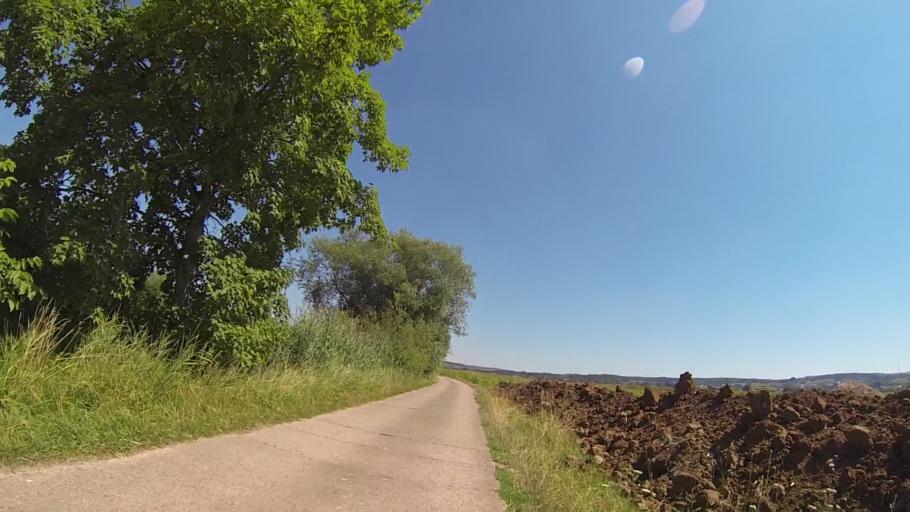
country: LU
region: Grevenmacher
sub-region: Canton de Remich
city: Remich
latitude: 49.5366
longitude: 6.3645
